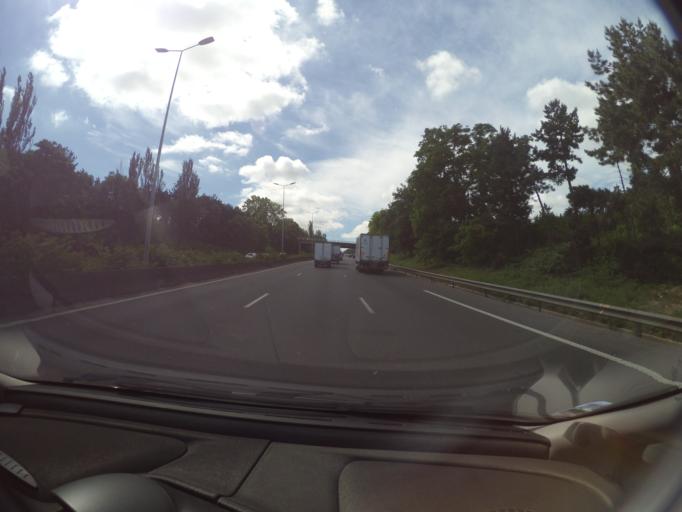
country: FR
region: Ile-de-France
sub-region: Departement du Val-de-Marne
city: Gentilly
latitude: 48.8052
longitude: 2.3418
